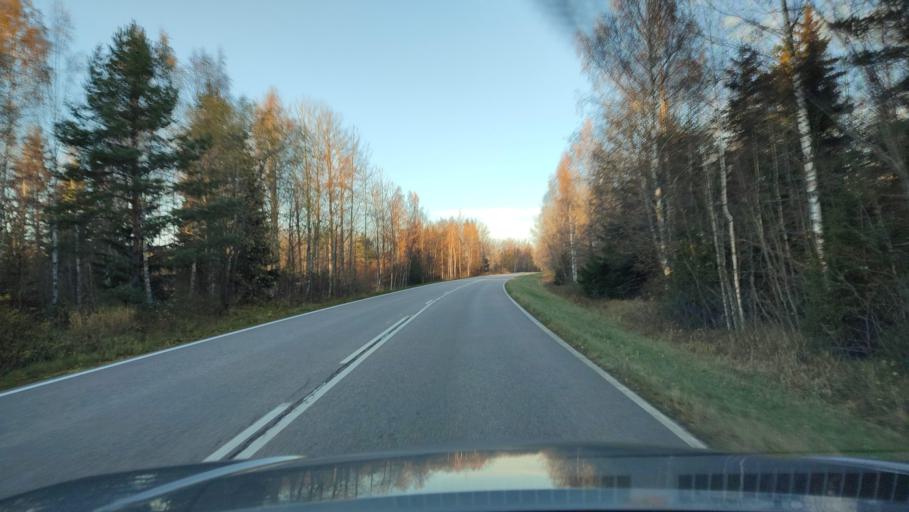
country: FI
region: Ostrobothnia
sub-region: Sydosterbotten
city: Kristinestad
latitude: 62.2871
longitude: 21.3775
